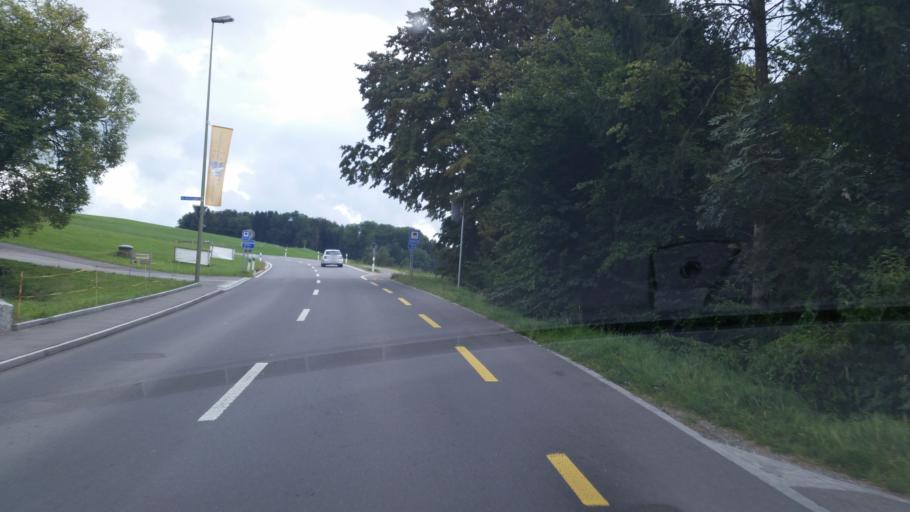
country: CH
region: Zurich
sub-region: Bezirk Affoltern
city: Mettmenstetten
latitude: 47.2453
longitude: 8.4720
